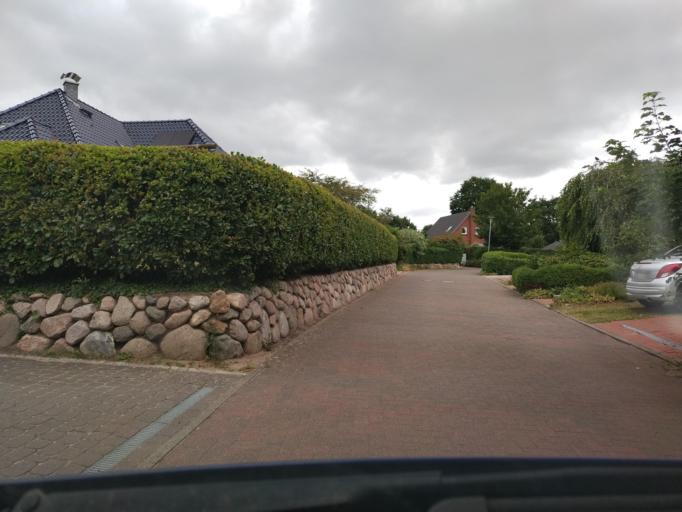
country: DE
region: Schleswig-Holstein
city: Husby
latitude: 54.4989
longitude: 9.4800
